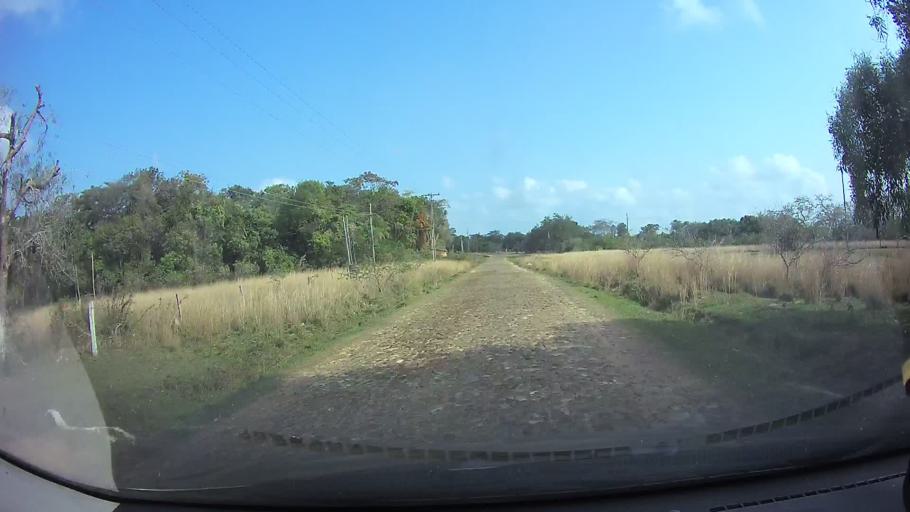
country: PY
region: Cordillera
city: Arroyos y Esteros
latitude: -24.9989
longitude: -57.1948
